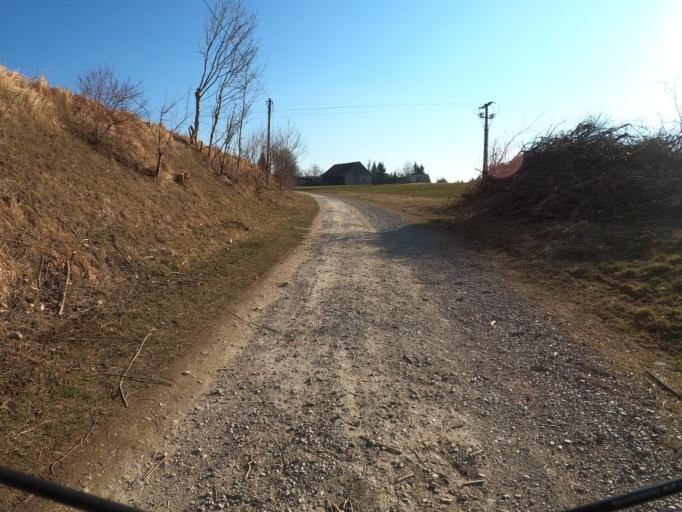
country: DE
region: Bavaria
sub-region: Swabia
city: Leipheim
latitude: 48.4404
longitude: 10.2210
